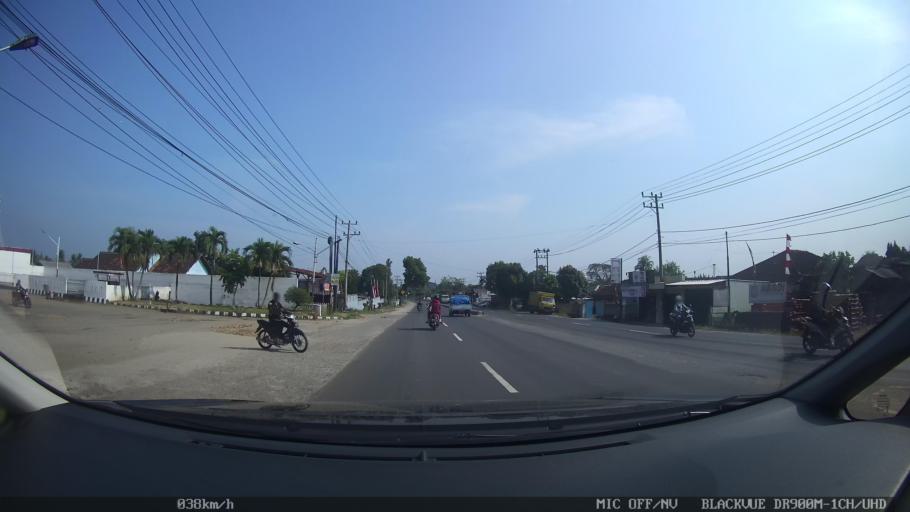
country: ID
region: Lampung
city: Natar
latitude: -5.2790
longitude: 105.1884
